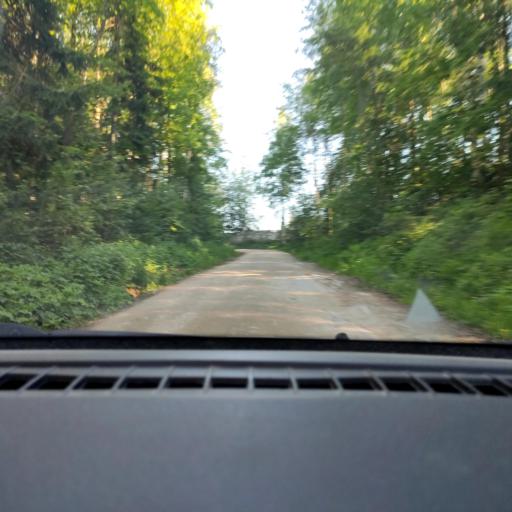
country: RU
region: Perm
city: Overyata
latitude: 58.1250
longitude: 55.8701
